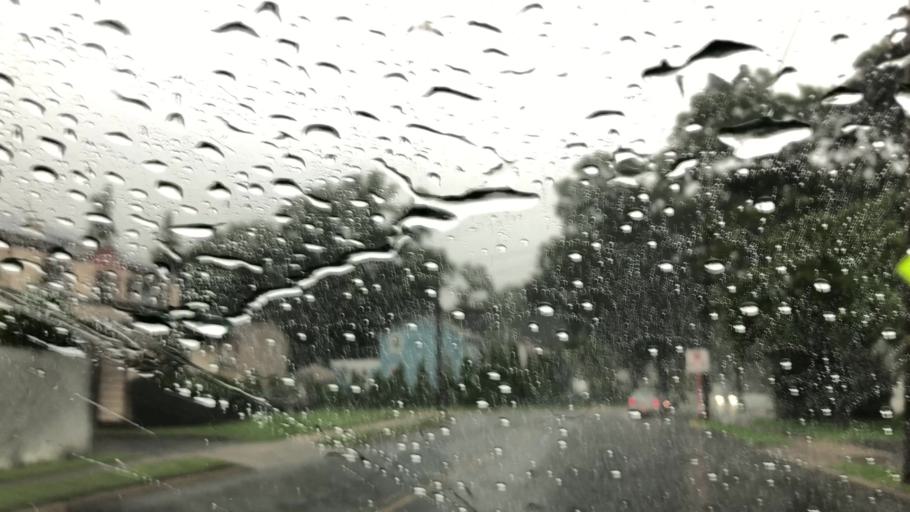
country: US
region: New Jersey
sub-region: Bergen County
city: Elmwood Park
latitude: 40.9177
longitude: -74.1157
